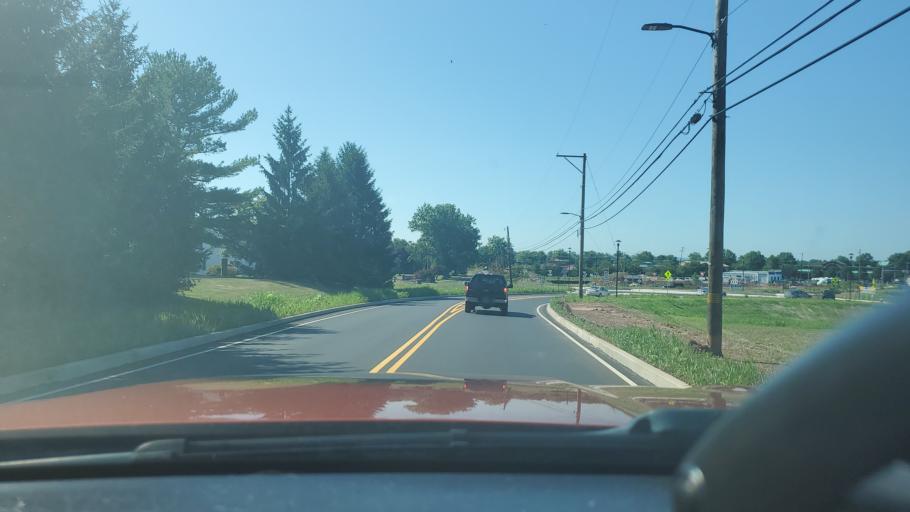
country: US
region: Pennsylvania
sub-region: Montgomery County
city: Limerick
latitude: 40.2357
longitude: -75.5263
